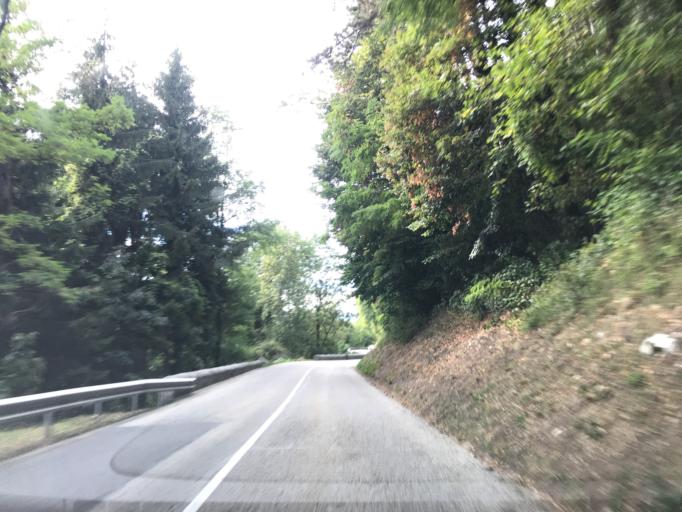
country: FR
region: Rhone-Alpes
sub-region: Departement de la Haute-Savoie
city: Menthon-Saint-Bernard
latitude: 45.8675
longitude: 6.1925
